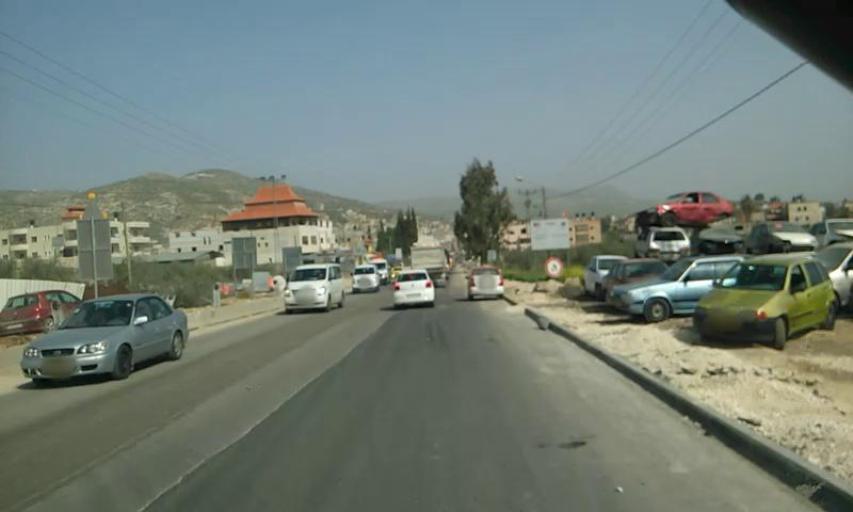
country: PS
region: West Bank
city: Huwwarah
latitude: 32.1381
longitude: 35.2580
